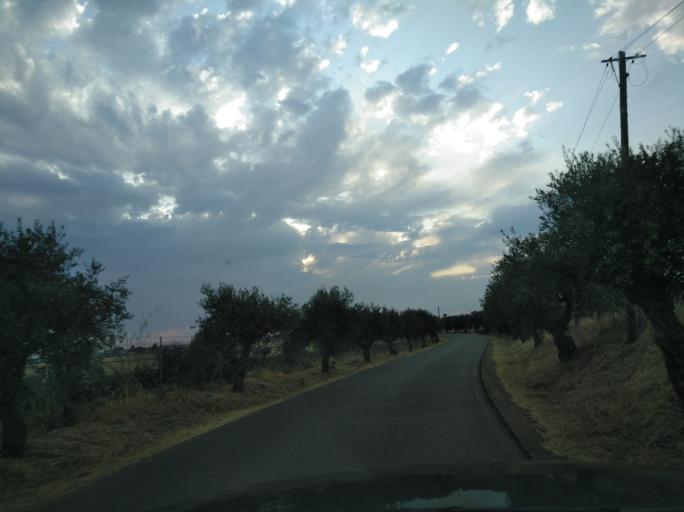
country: PT
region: Portalegre
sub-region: Campo Maior
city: Campo Maior
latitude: 39.0168
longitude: -7.0458
